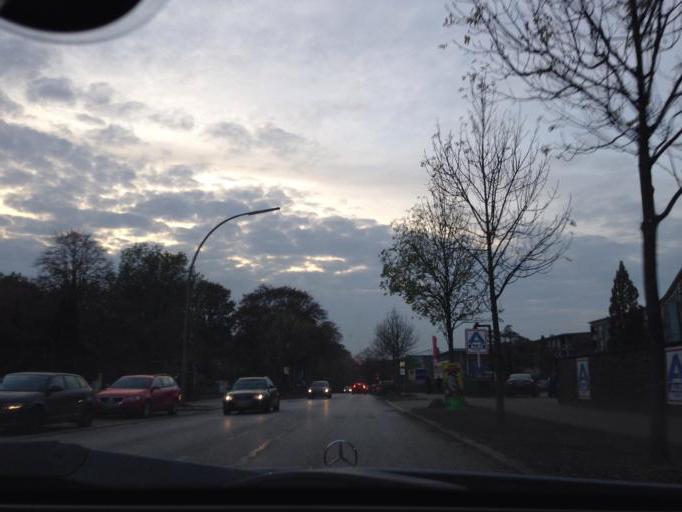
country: DE
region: Hamburg
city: Farmsen-Berne
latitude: 53.6002
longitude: 10.1394
